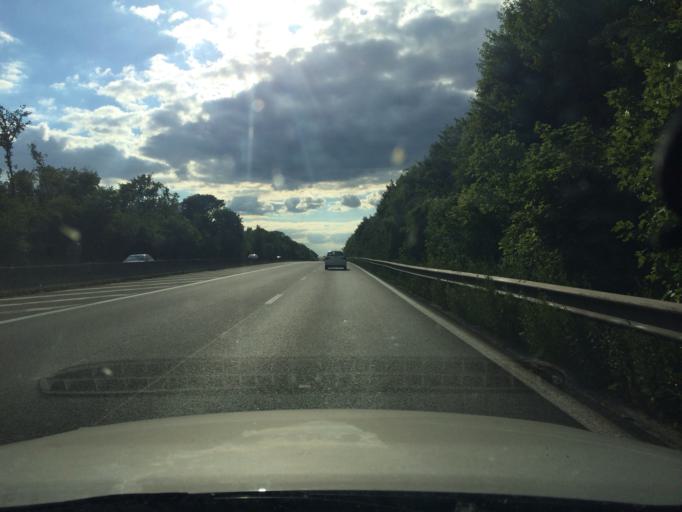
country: FR
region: Lorraine
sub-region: Departement de Meurthe-et-Moselle
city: Ludres
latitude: 48.6436
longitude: 6.1563
